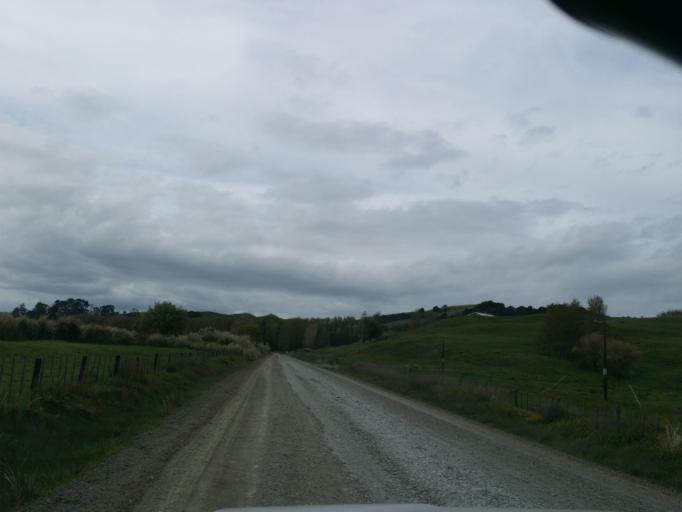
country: NZ
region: Northland
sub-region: Kaipara District
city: Dargaville
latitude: -35.9269
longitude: 173.9211
